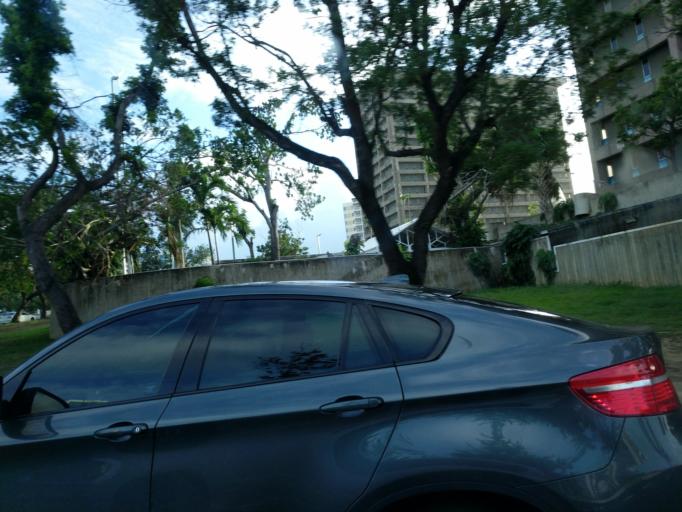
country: PR
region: San Juan
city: San Juan
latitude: 18.4499
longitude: -66.0666
